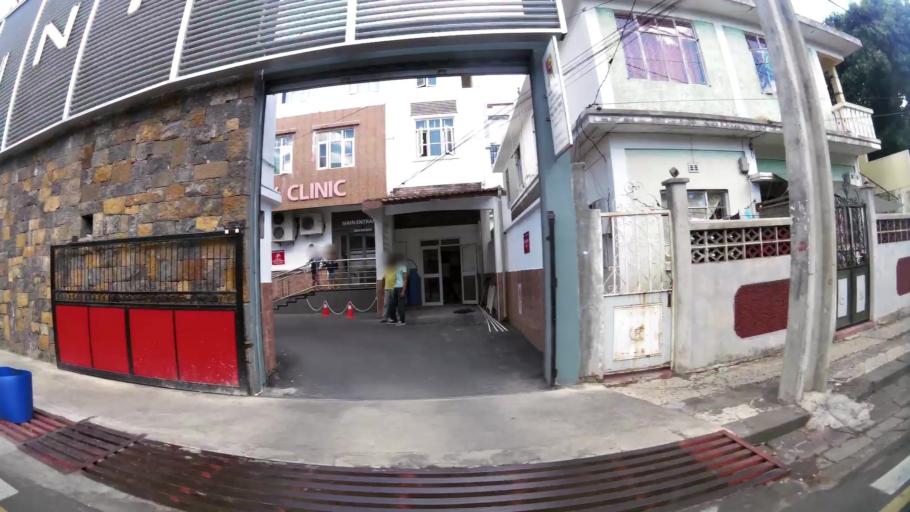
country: MU
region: Port Louis
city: Port Louis
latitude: -20.1623
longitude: 57.5146
